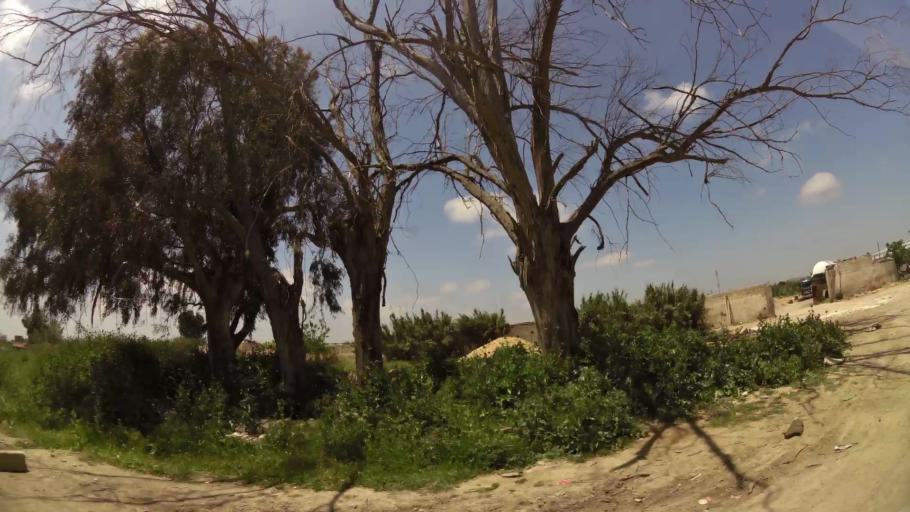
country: MA
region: Fes-Boulemane
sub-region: Fes
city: Fes
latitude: 34.0389
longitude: -5.0607
